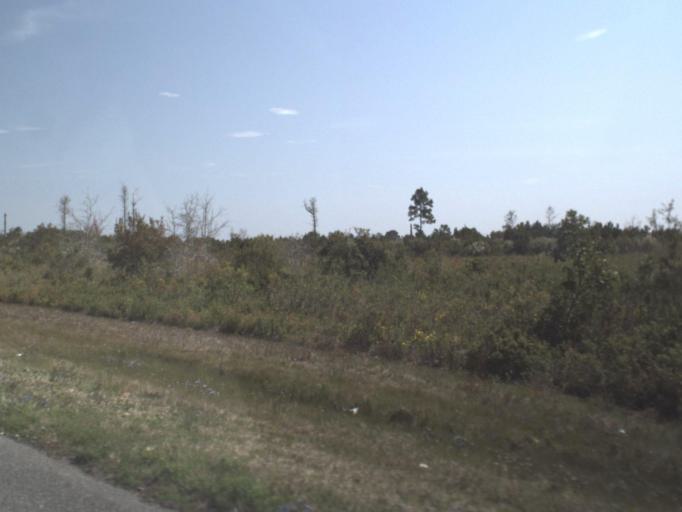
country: US
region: Florida
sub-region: Franklin County
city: Apalachicola
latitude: 29.7246
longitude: -85.0785
